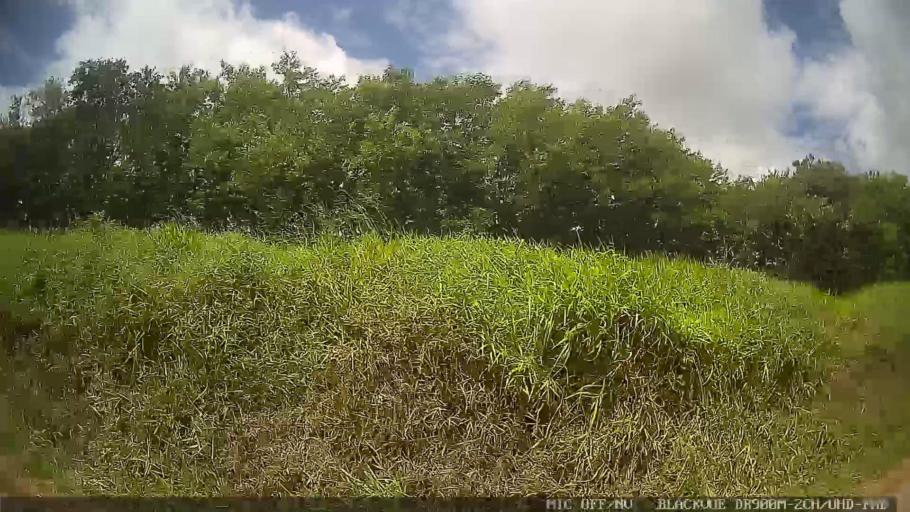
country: BR
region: Sao Paulo
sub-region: Braganca Paulista
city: Braganca Paulista
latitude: -22.7988
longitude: -46.5041
